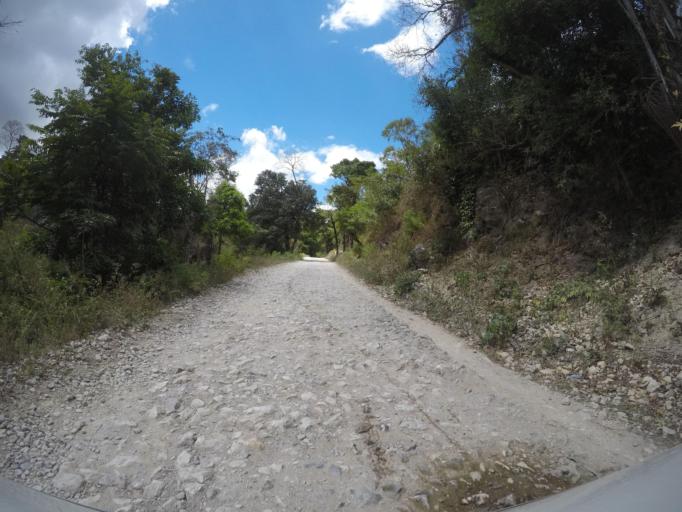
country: TL
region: Baucau
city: Baucau
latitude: -8.5273
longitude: 126.6934
